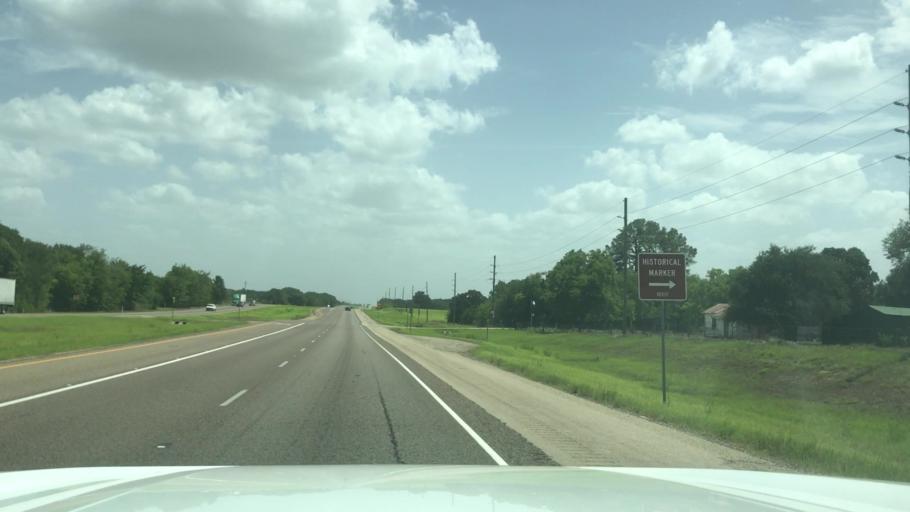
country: US
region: Texas
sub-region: Robertson County
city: Calvert
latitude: 31.0961
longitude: -96.7152
